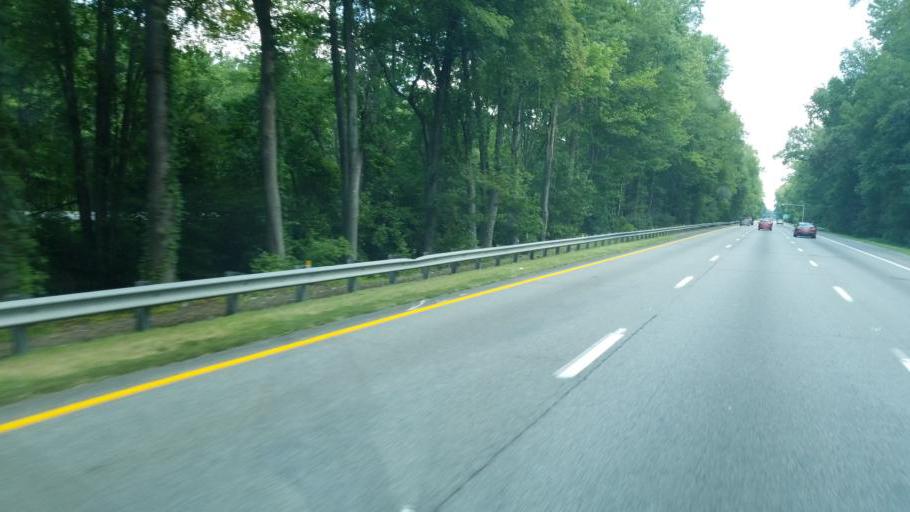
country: US
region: Virginia
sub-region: City of Suffolk
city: Suffolk
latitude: 36.7596
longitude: -76.4981
